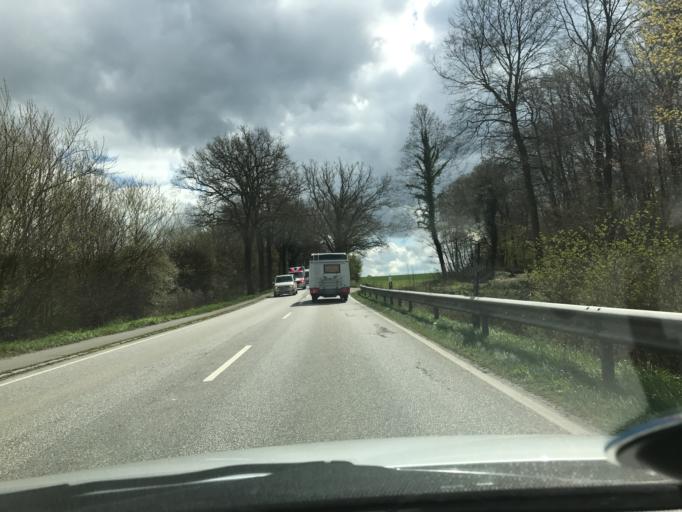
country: DE
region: Schleswig-Holstein
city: Susel
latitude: 54.0989
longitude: 10.6736
